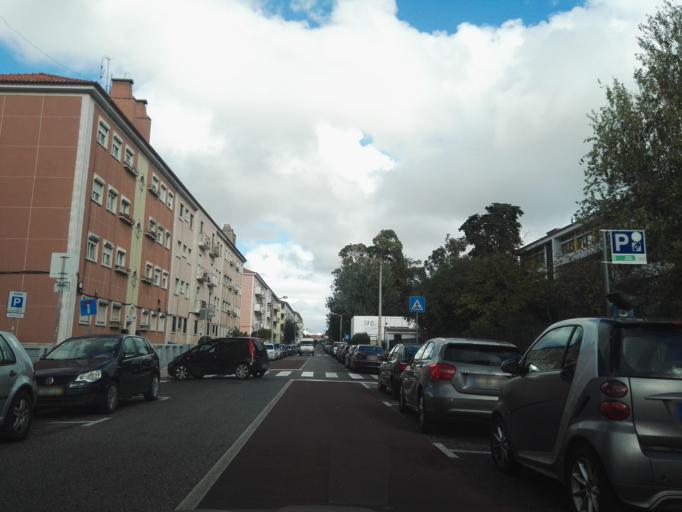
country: PT
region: Lisbon
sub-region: Lisbon
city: Lisbon
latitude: 38.7517
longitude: -9.1413
